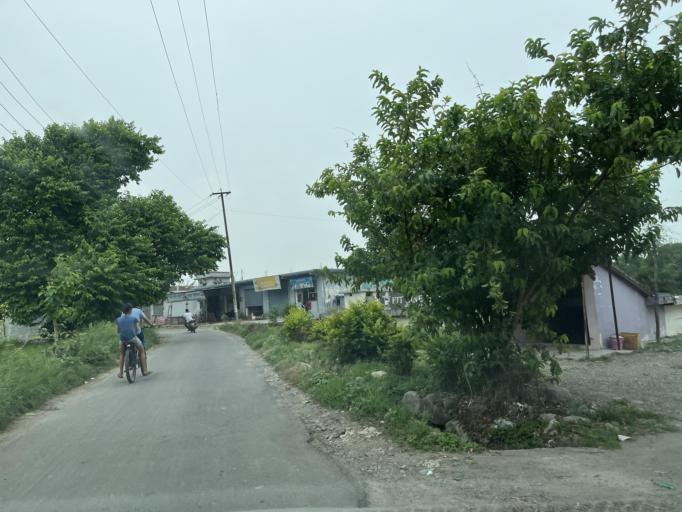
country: IN
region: Uttarakhand
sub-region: Naini Tal
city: Haldwani
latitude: 29.1711
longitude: 79.4841
